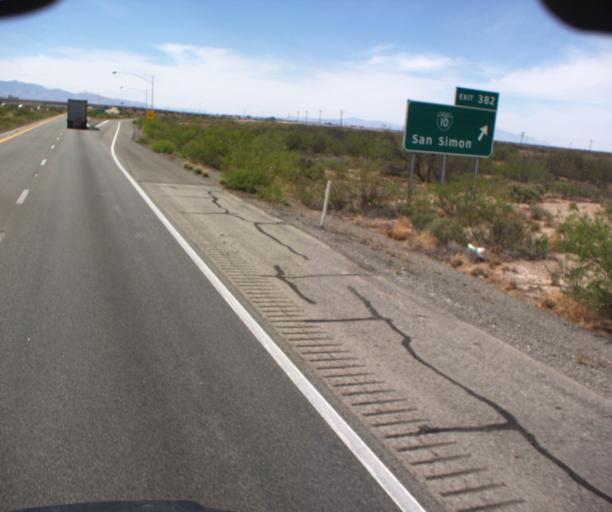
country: US
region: New Mexico
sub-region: Hidalgo County
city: Lordsburg
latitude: 32.2575
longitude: -109.1908
